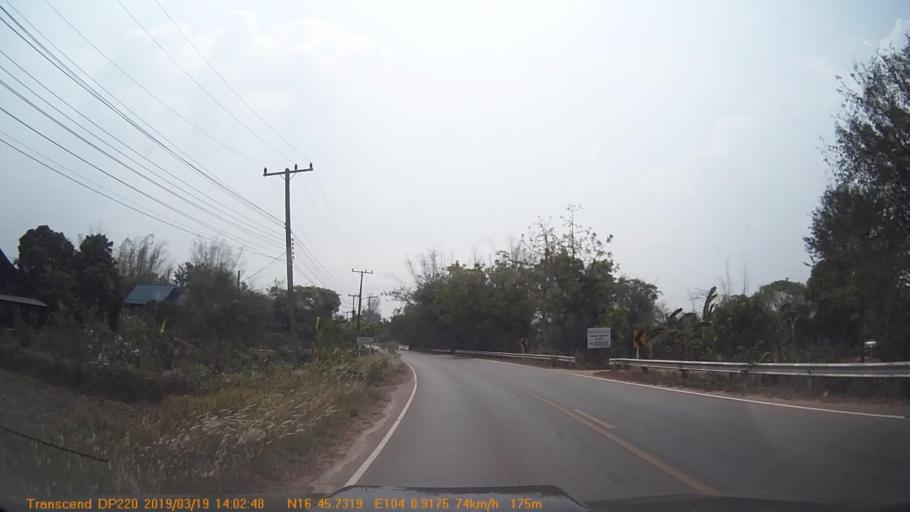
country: TH
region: Kalasin
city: Na Khu
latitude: 16.7621
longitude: 104.0149
